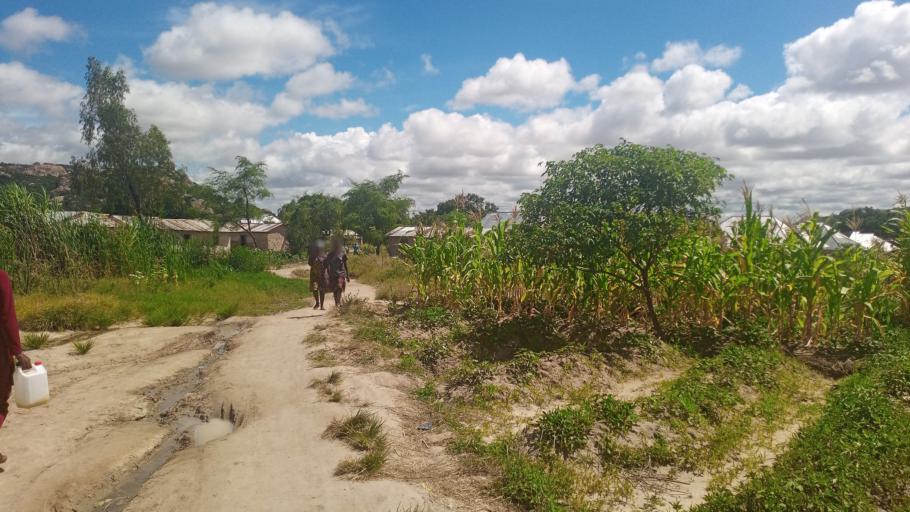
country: TZ
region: Dodoma
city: Dodoma
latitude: -6.1932
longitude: 35.7241
